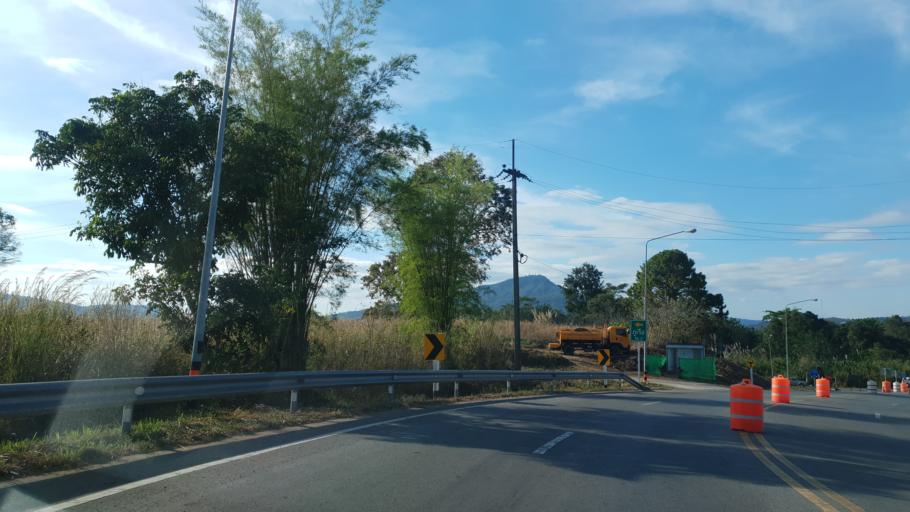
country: TH
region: Loei
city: Phu Ruea
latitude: 17.4466
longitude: 101.4916
